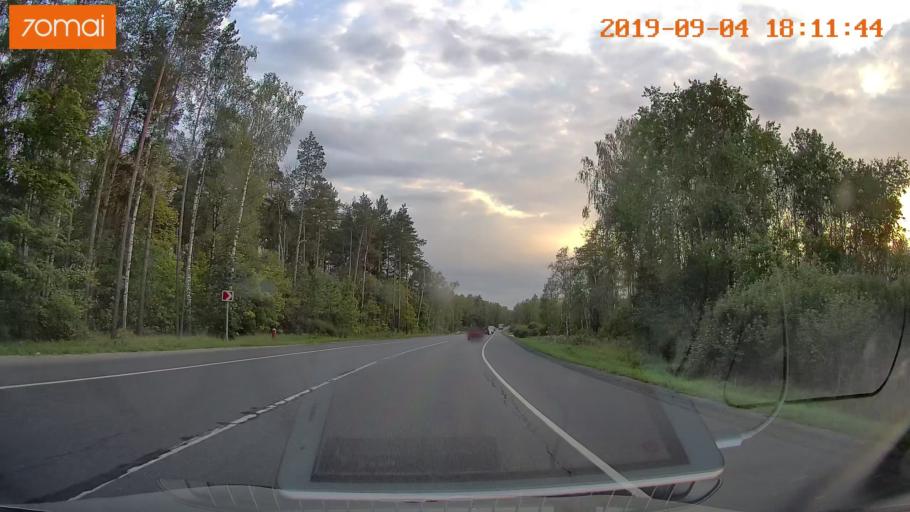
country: RU
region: Moskovskaya
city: Lopatinskiy
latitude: 55.3752
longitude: 38.7514
